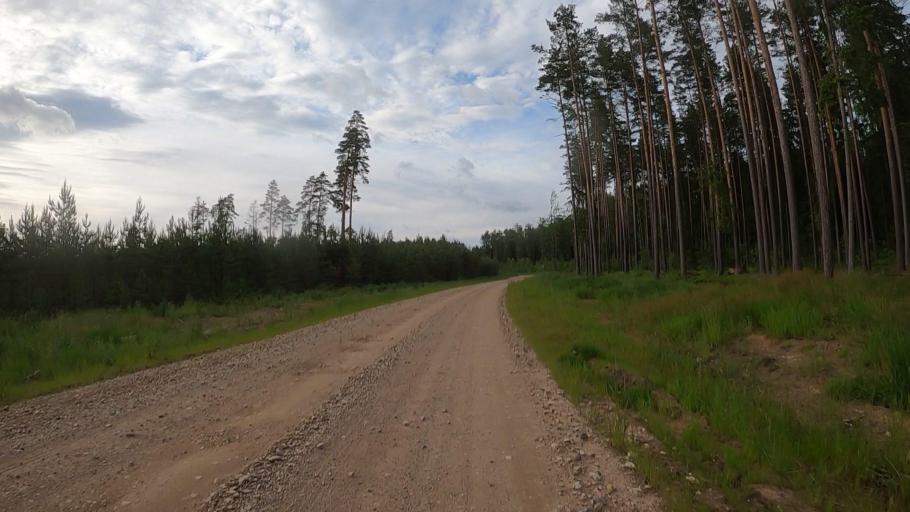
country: LV
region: Olaine
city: Olaine
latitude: 56.7687
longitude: 23.9034
